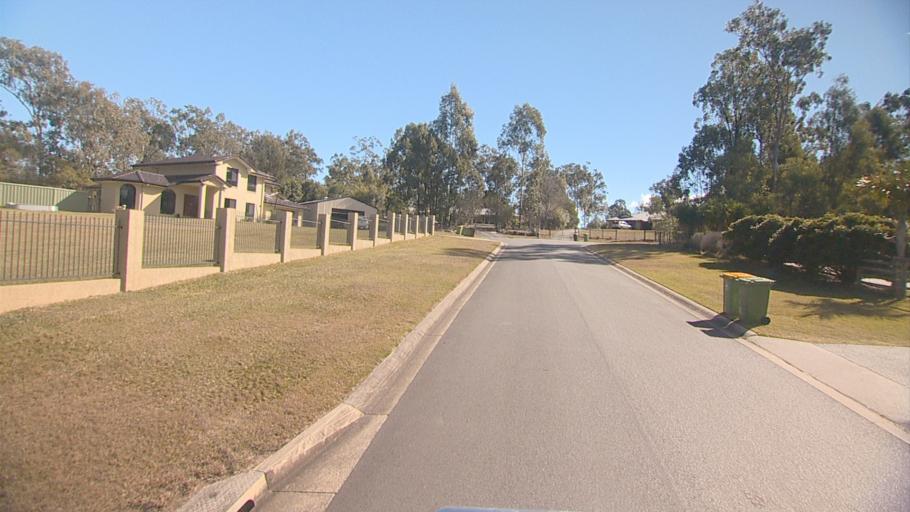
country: AU
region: Queensland
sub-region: Logan
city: North Maclean
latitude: -27.7531
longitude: 152.9406
